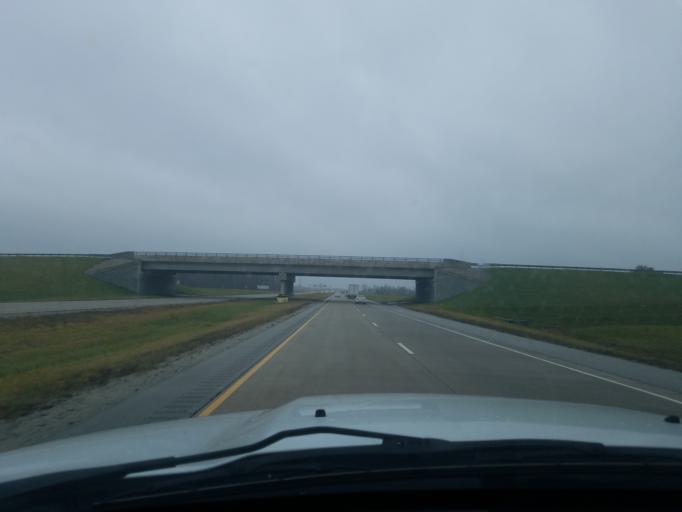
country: US
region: Indiana
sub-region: Howard County
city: Kokomo
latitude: 40.4639
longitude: -86.0812
